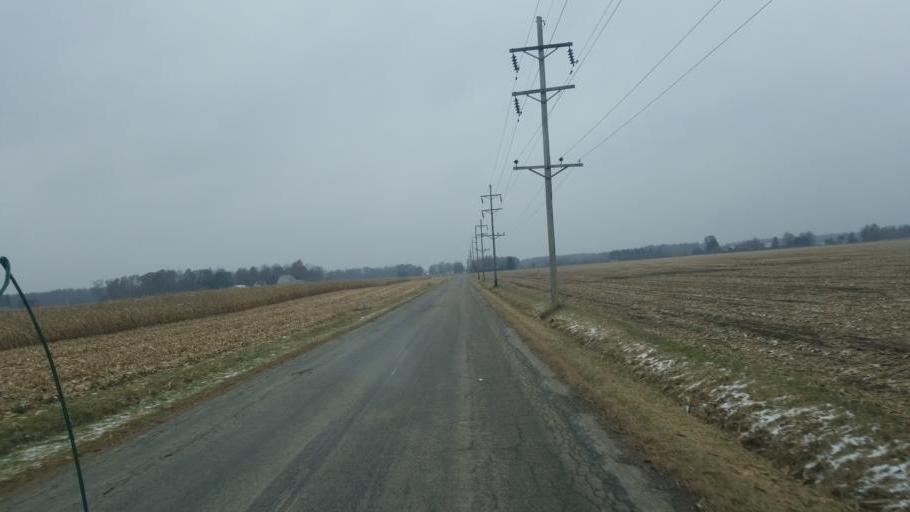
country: US
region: Ohio
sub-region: Richland County
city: Shelby
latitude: 40.9234
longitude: -82.6860
